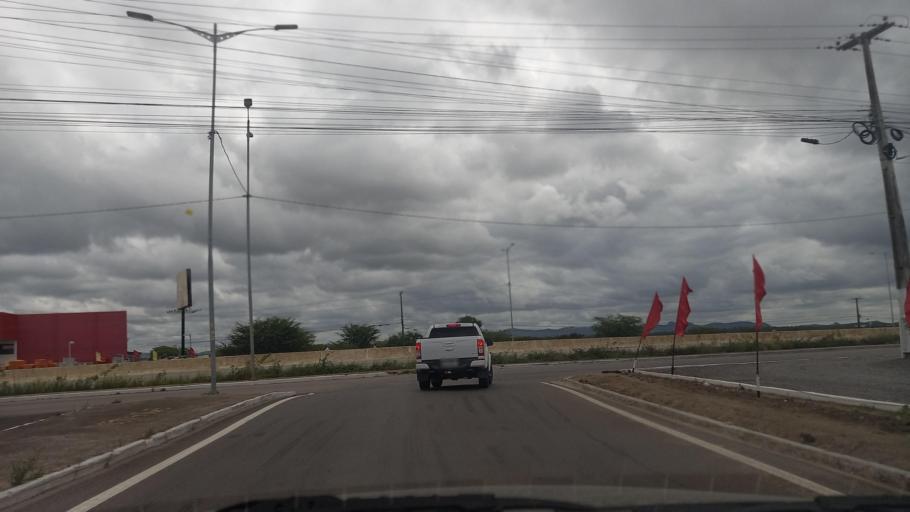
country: BR
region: Pernambuco
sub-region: Caruaru
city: Caruaru
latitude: -8.2525
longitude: -35.9747
